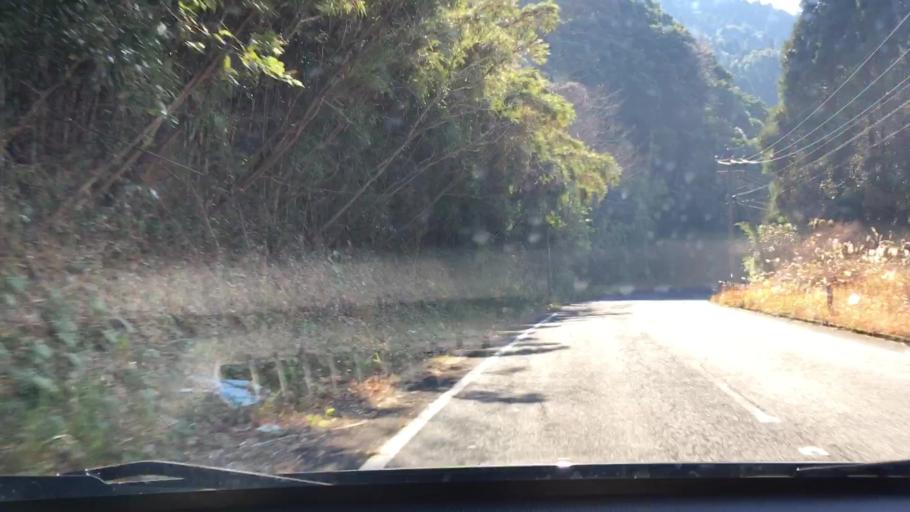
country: JP
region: Kagoshima
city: Kokubu-matsuki
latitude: 31.6704
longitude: 130.8307
